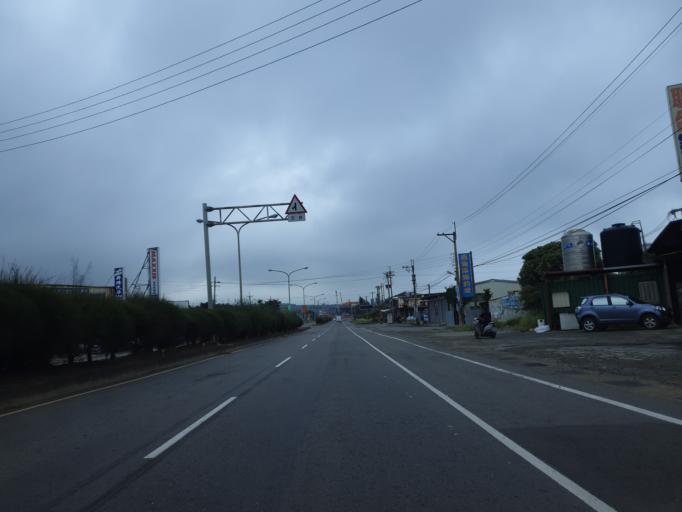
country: TW
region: Taiwan
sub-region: Hsinchu
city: Zhubei
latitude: 24.9059
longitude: 120.9752
